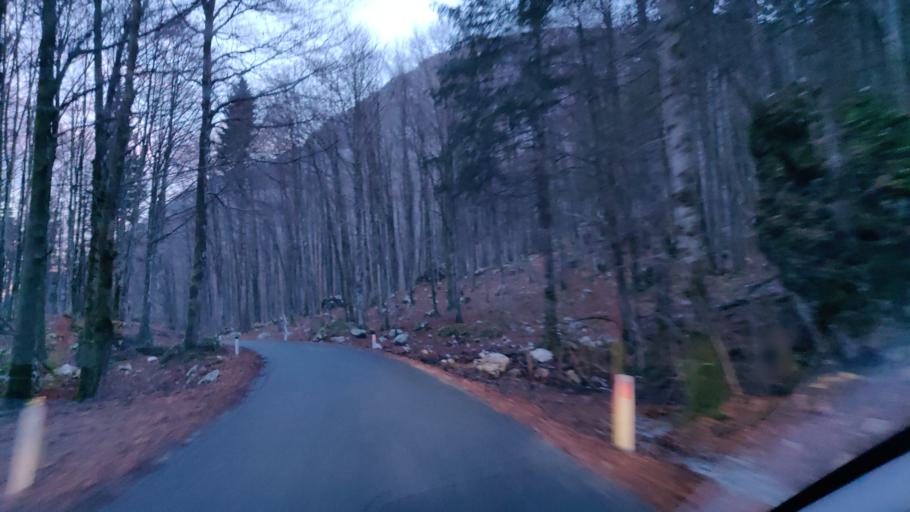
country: SI
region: Tolmin
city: Tolmin
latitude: 46.2774
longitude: 13.8130
